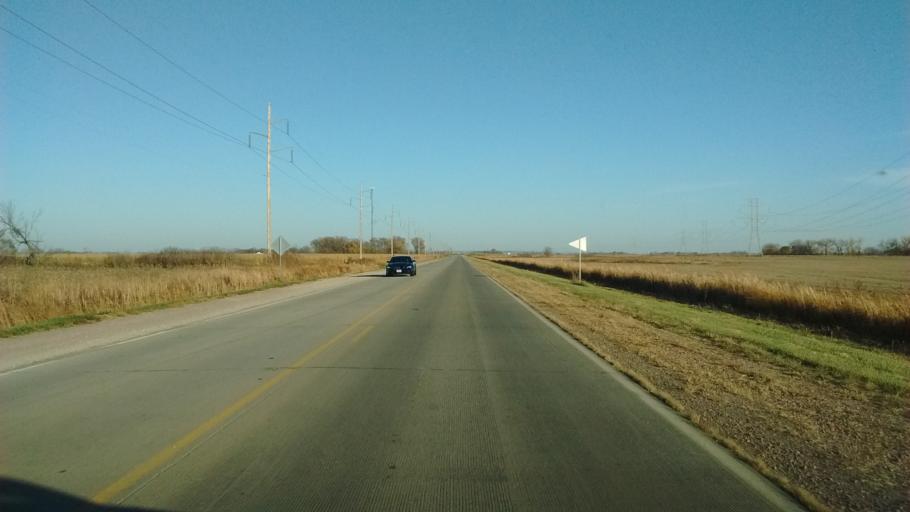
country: US
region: Iowa
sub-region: Woodbury County
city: Sergeant Bluff
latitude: 42.3301
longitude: -96.3464
